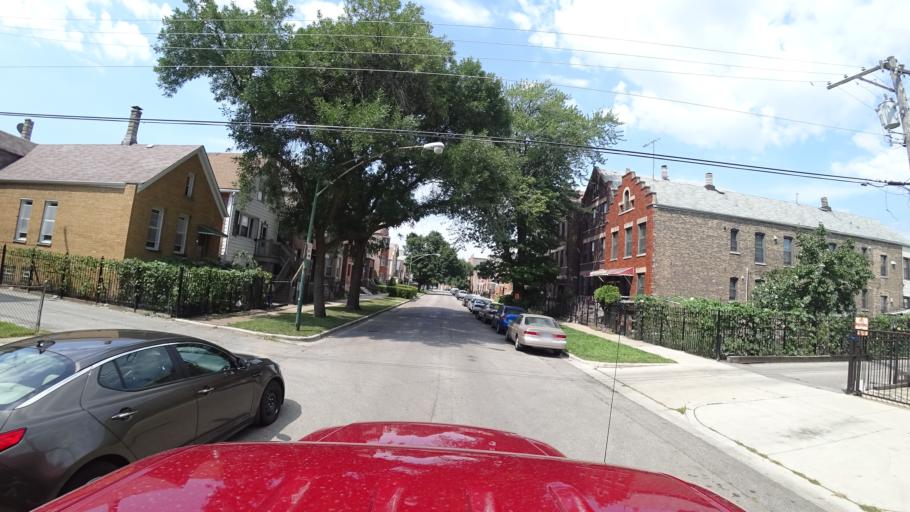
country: US
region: Illinois
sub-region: Cook County
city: Chicago
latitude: 41.8372
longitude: -87.6490
